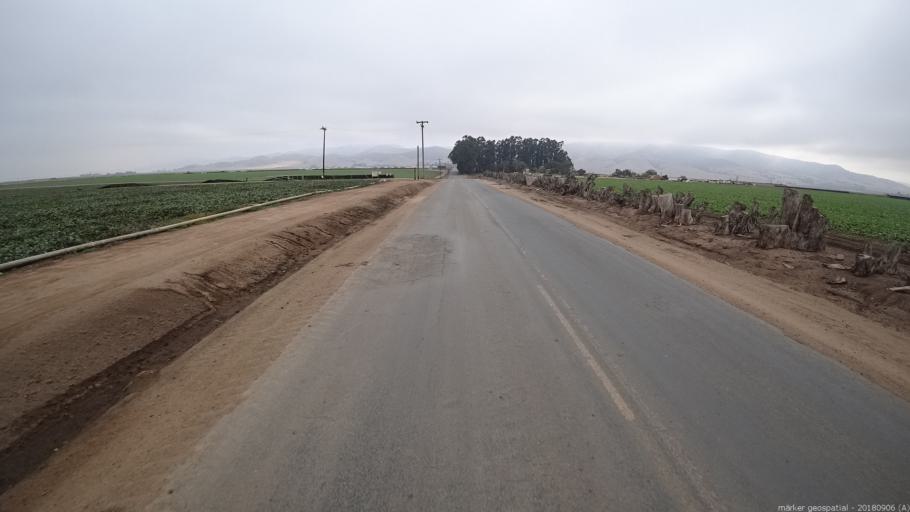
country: US
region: California
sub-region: Monterey County
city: Chualar
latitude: 36.6500
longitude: -121.5630
